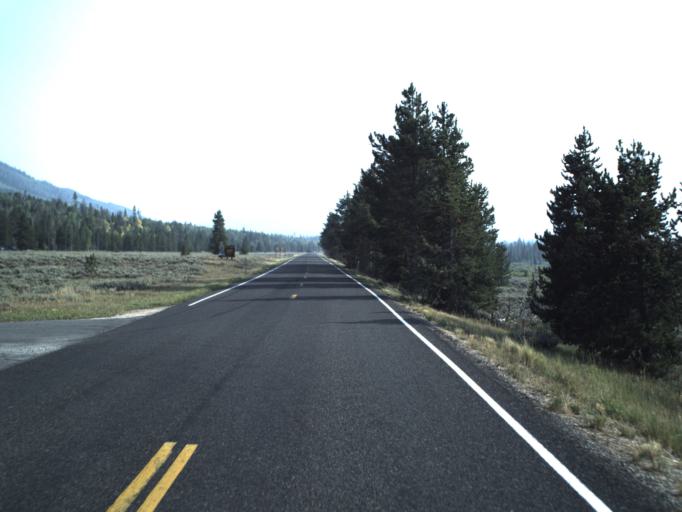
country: US
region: Wyoming
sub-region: Uinta County
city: Evanston
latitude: 40.8840
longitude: -110.8321
